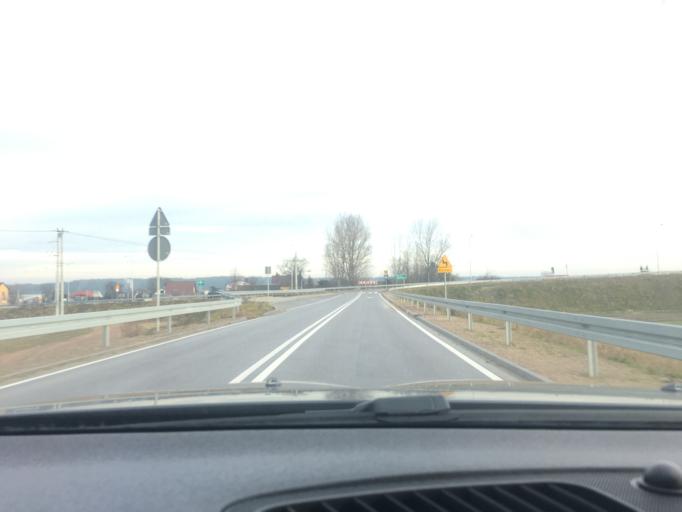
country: PL
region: Swietokrzyskie
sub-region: Powiat jedrzejowski
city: Jedrzejow
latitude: 50.6600
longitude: 20.3278
